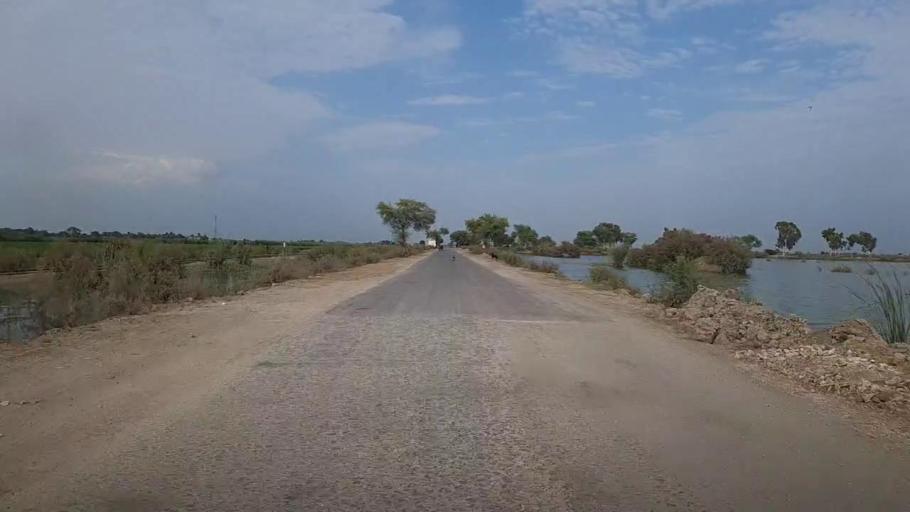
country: PK
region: Sindh
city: Thul
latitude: 28.2798
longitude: 68.8523
